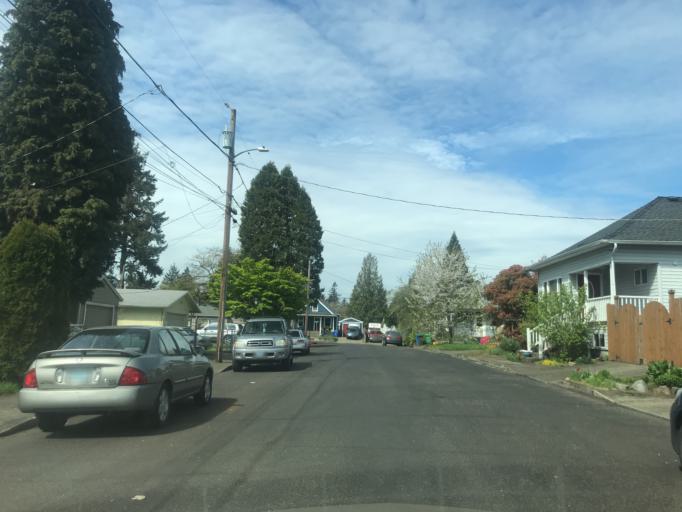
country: US
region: Oregon
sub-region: Multnomah County
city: Lents
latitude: 45.4837
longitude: -122.5947
